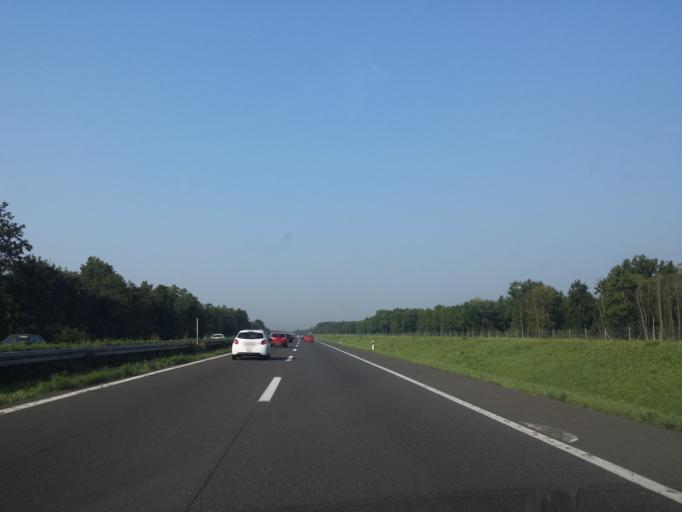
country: HR
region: Zagrebacka
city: Jastrebarsko
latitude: 45.6595
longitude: 15.7048
